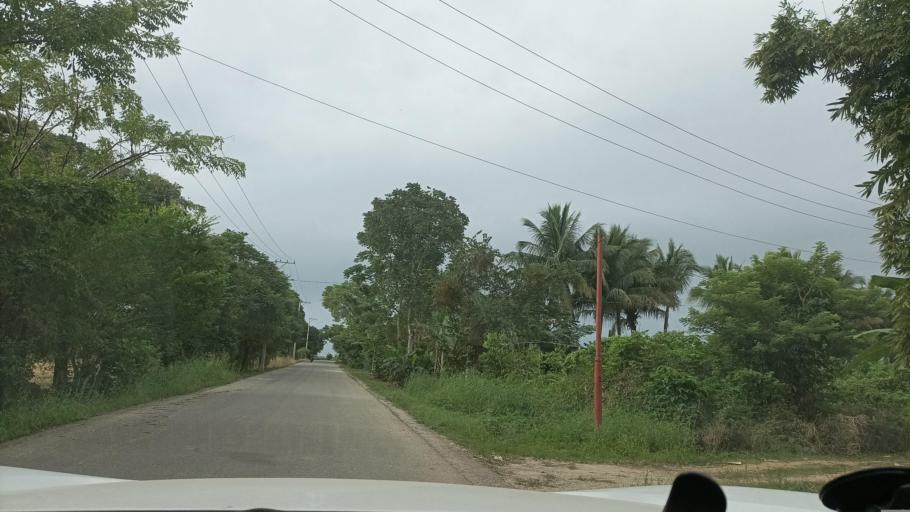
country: MX
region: Veracruz
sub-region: Jaltipan
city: Las Lomas de Tacamichapan
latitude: 17.8628
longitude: -94.7113
